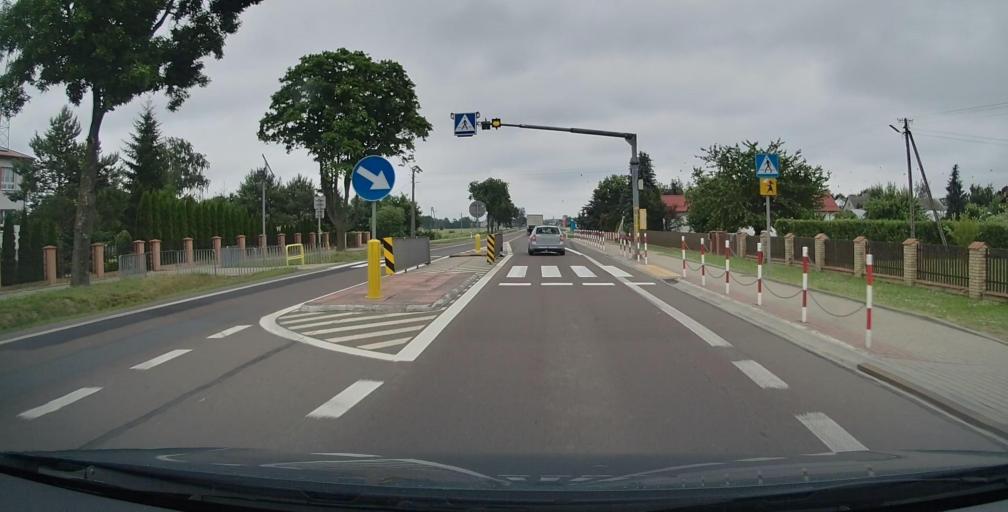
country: PL
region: Lublin Voivodeship
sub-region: Powiat bialski
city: Rzeczyca
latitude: 52.0268
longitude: 22.7126
